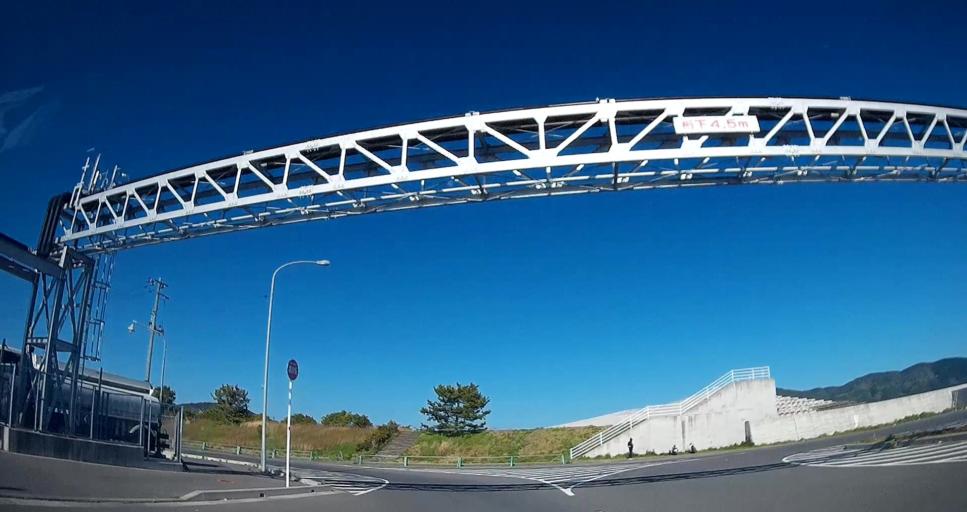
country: JP
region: Miyagi
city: Ishinomaki
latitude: 38.4140
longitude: 141.3400
